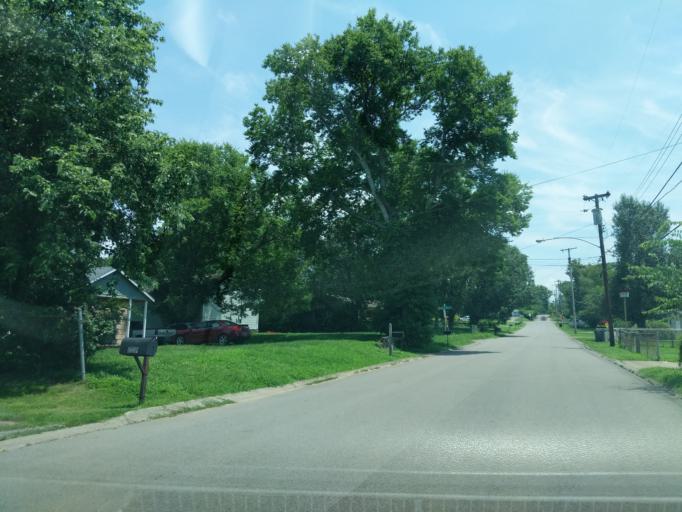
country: US
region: Tennessee
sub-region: Davidson County
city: Lakewood
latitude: 36.2381
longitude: -86.6335
